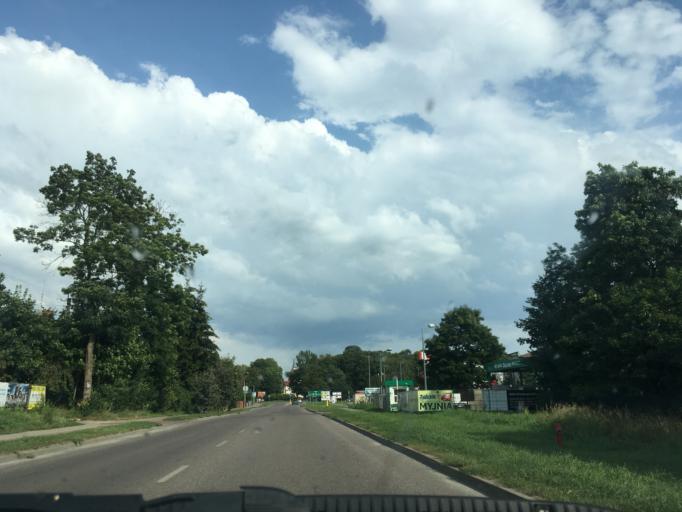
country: PL
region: Warmian-Masurian Voivodeship
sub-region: Powiat olecki
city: Olecko
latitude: 54.0406
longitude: 22.4930
